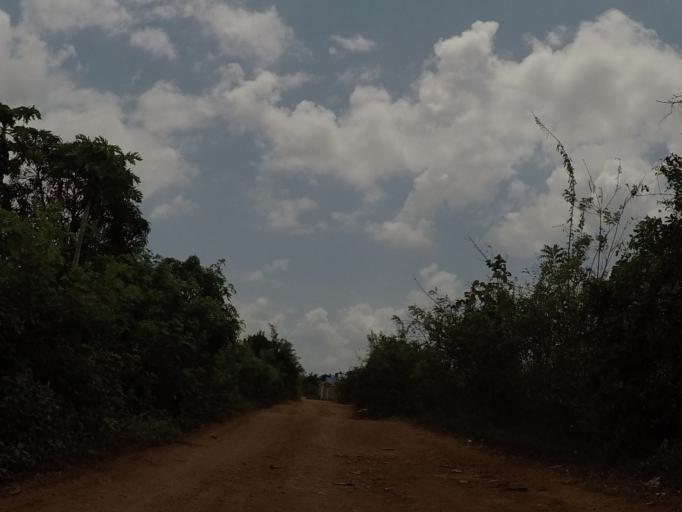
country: TZ
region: Zanzibar Central/South
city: Koani
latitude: -6.1876
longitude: 39.3090
